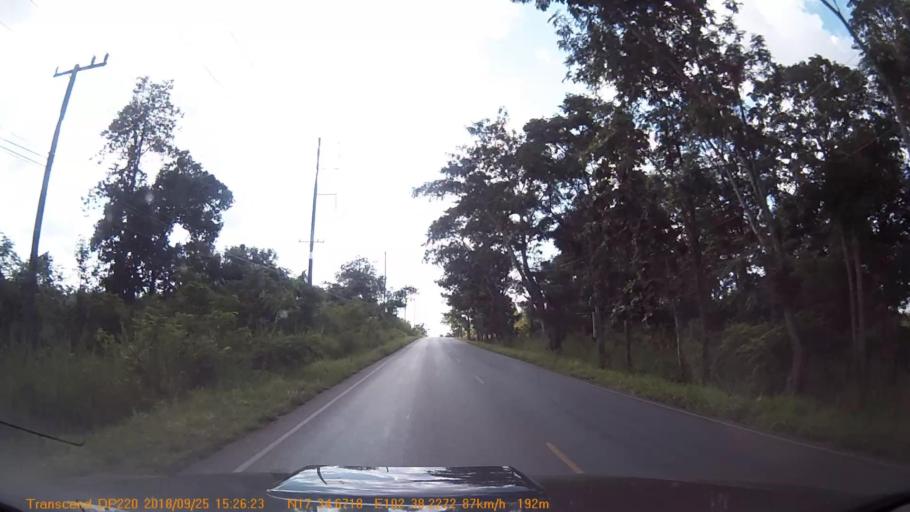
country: TH
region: Nong Khai
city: Sa Khrai
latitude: 17.5780
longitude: 102.6369
